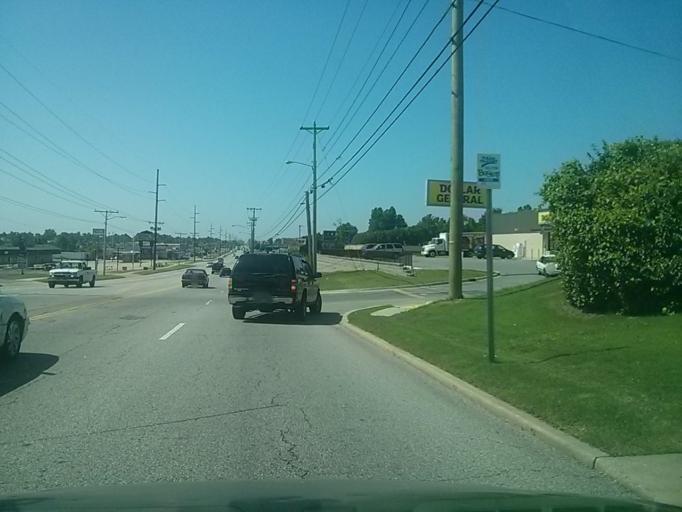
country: US
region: Oklahoma
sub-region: Tulsa County
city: Tulsa
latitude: 36.1403
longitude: -95.9047
